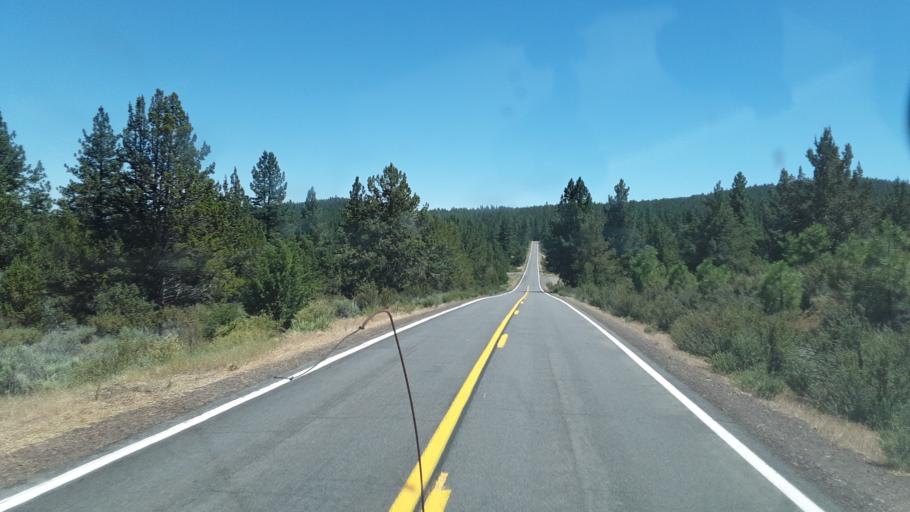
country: US
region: California
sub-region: Lassen County
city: Johnstonville
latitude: 40.4990
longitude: -120.5623
